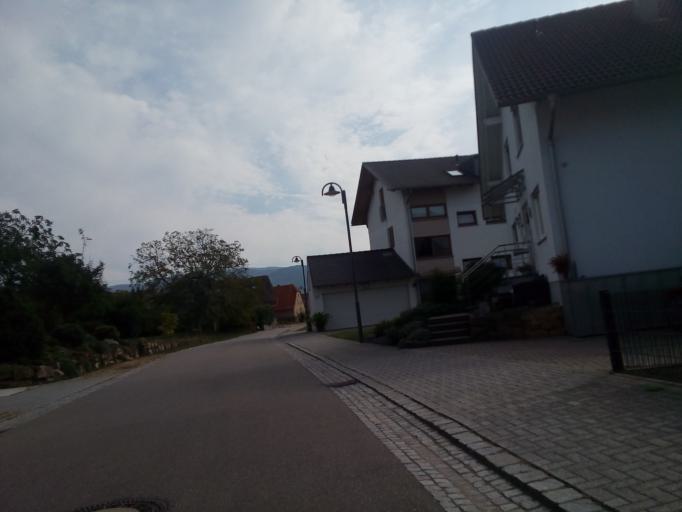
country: DE
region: Baden-Wuerttemberg
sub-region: Freiburg Region
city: Sasbach
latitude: 48.6597
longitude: 8.0835
